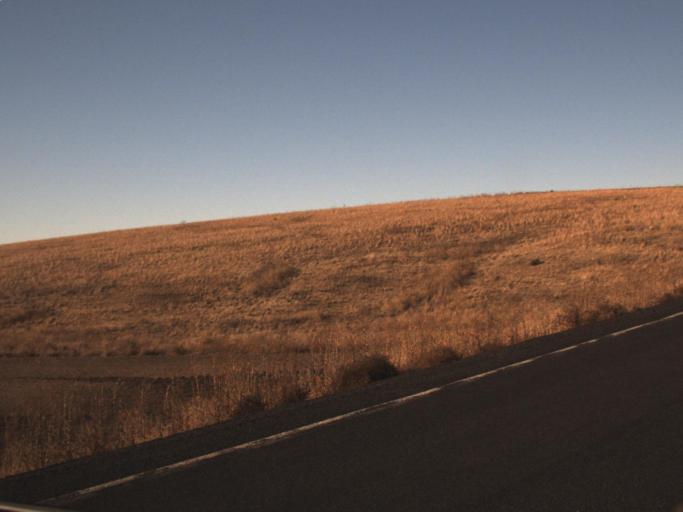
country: US
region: Washington
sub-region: Adams County
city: Ritzville
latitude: 47.0875
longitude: -118.3654
